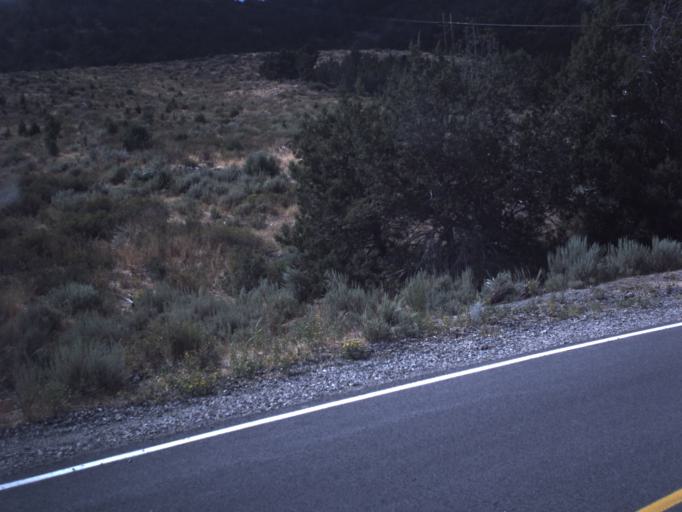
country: US
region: Utah
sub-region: Tooele County
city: Grantsville
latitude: 40.3463
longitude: -112.5655
